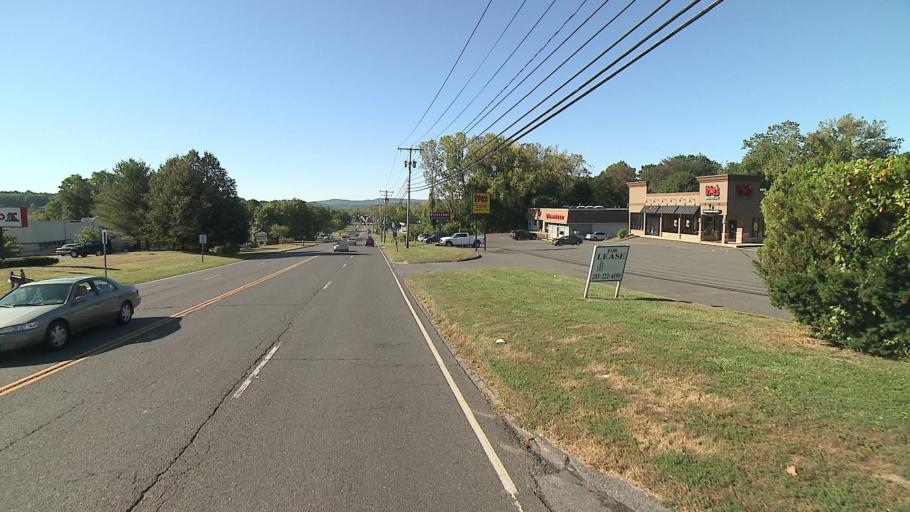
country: US
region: Connecticut
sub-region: Fairfield County
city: Danbury
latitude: 41.4404
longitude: -73.4063
